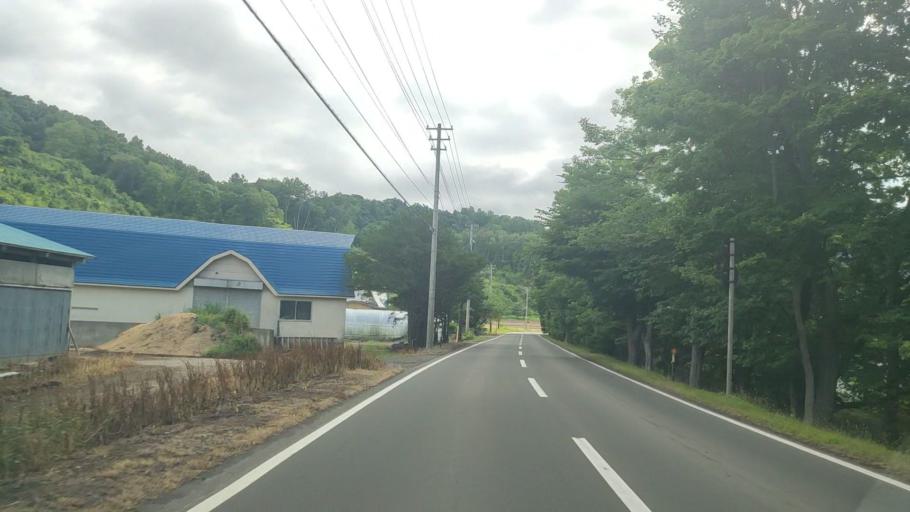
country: JP
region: Hokkaido
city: Date
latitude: 42.5593
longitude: 140.8771
